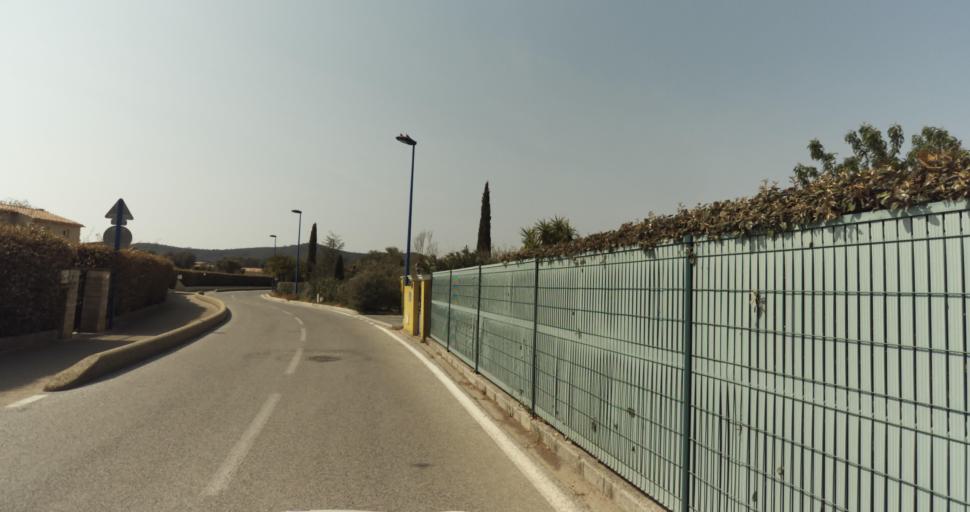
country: FR
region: Provence-Alpes-Cote d'Azur
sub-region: Departement du Var
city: Bormes-les-Mimosas
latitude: 43.1339
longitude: 6.3407
